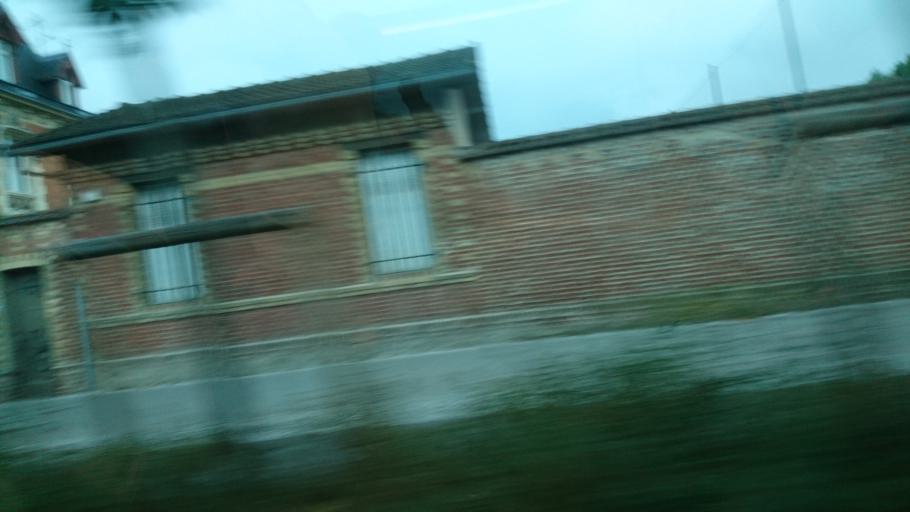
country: FR
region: Ile-de-France
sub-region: Departement de Seine-Saint-Denis
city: Saint-Denis
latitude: 48.9451
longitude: 2.3570
